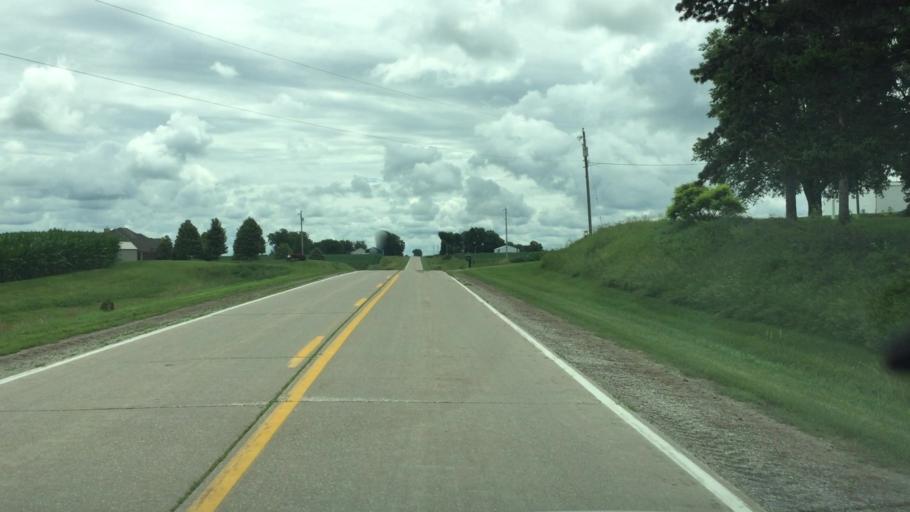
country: US
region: Iowa
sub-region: Jasper County
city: Monroe
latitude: 41.5807
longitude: -93.1202
